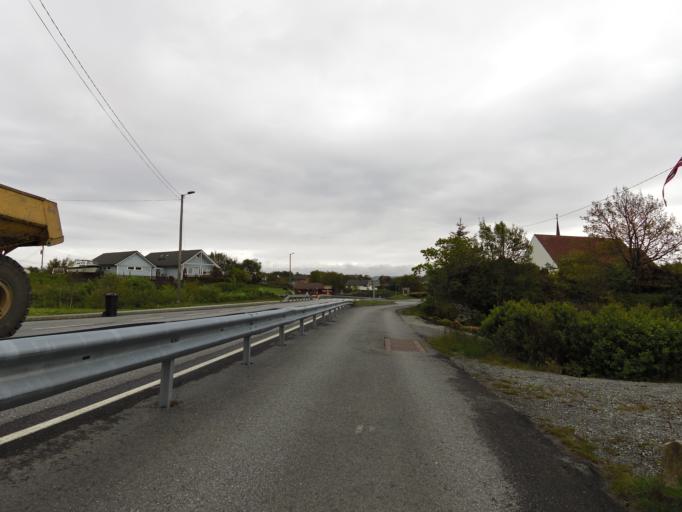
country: NO
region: Hordaland
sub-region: Sveio
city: Sveio
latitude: 59.6051
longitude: 5.2097
